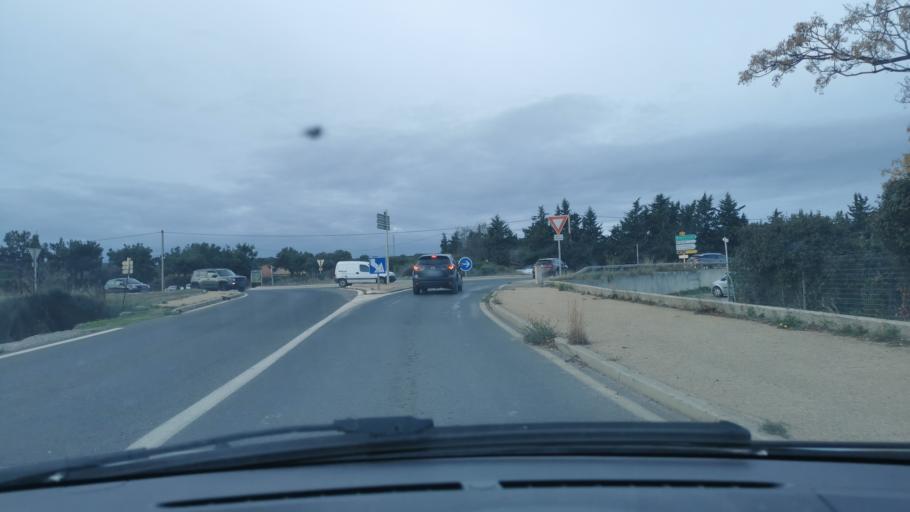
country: FR
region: Languedoc-Roussillon
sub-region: Departement de l'Herault
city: Vic-la-Gardiole
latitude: 43.5005
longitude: 3.7868
